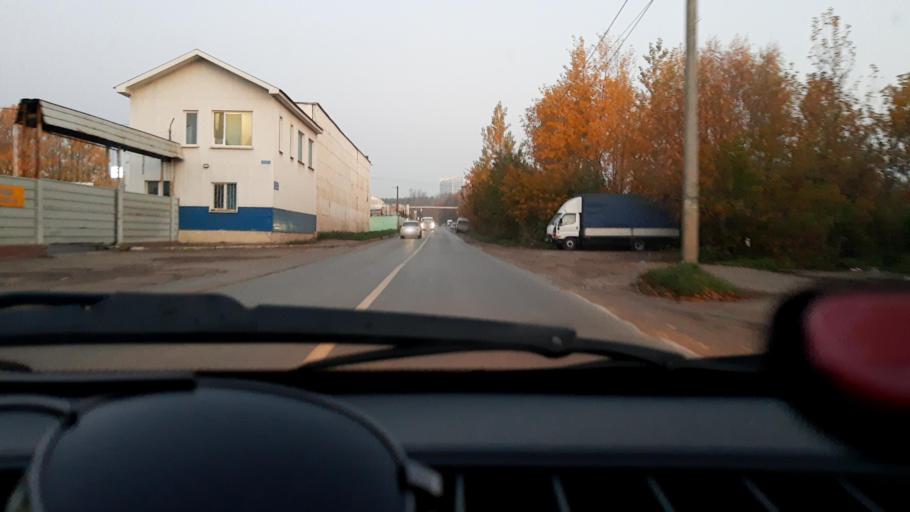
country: RU
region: Bashkortostan
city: Ufa
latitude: 54.8061
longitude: 56.0700
